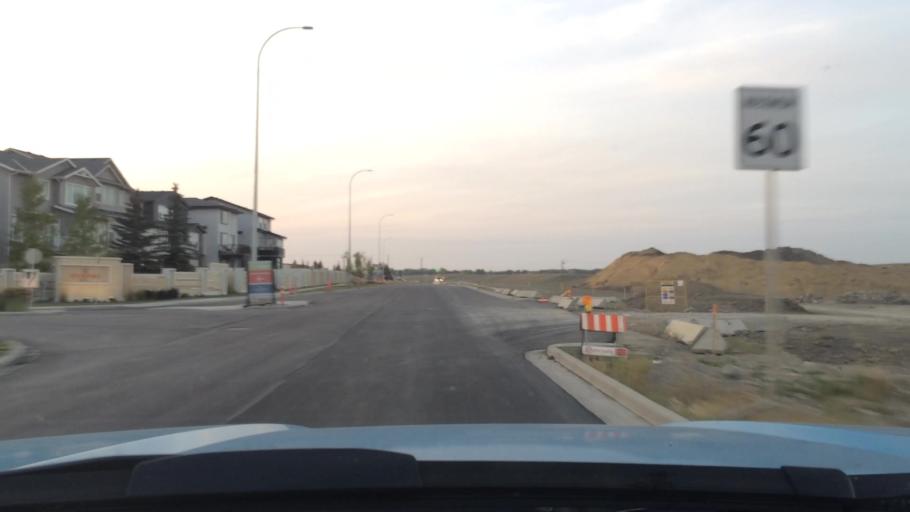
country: CA
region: Alberta
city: Calgary
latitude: 51.1804
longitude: -114.1338
